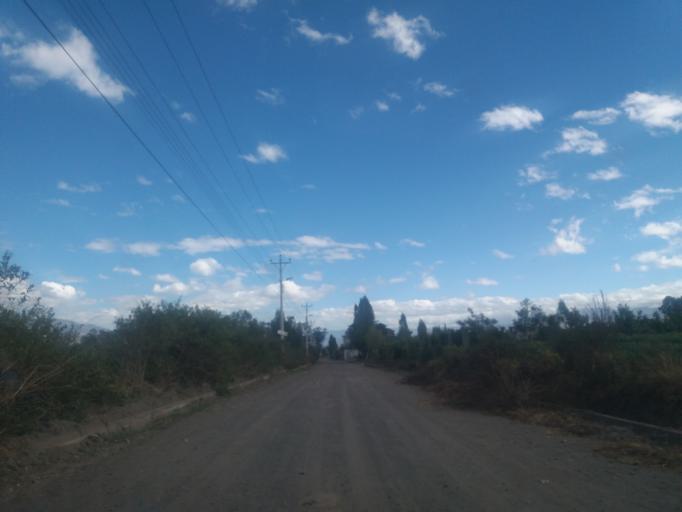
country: EC
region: Pichincha
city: Sangolqui
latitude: -0.1807
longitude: -78.3366
